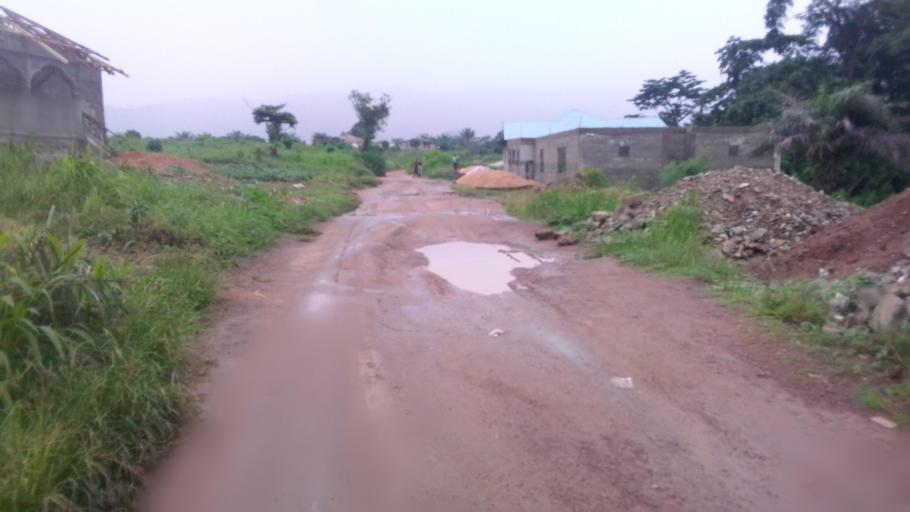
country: SL
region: Eastern Province
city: Kenema
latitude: 7.9015
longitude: -11.1634
